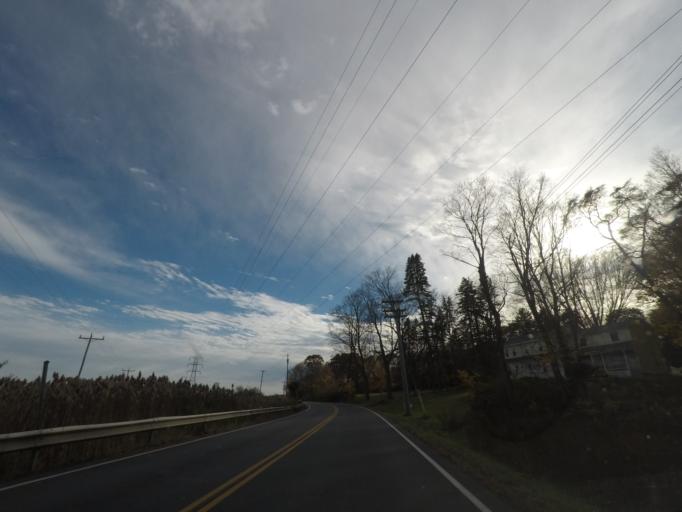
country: US
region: New York
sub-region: Albany County
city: Voorheesville
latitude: 42.6170
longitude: -73.9077
